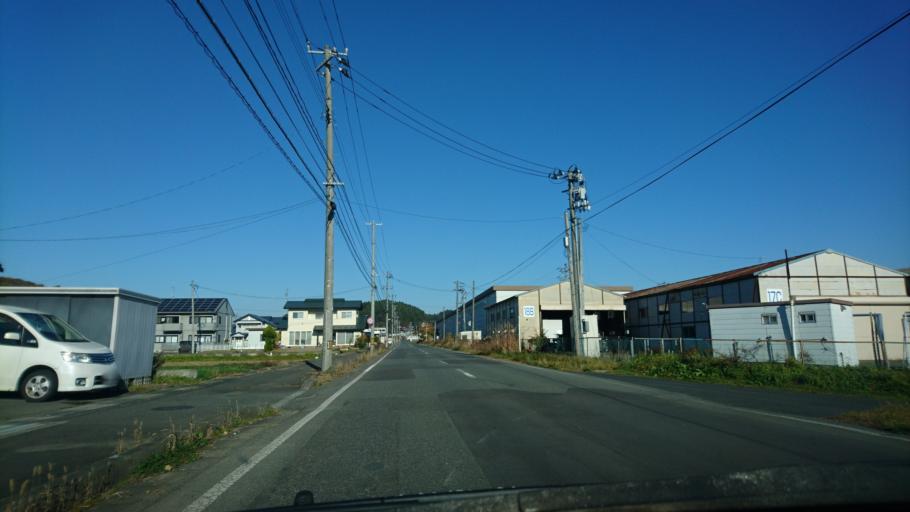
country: JP
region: Iwate
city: Mizusawa
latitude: 39.0364
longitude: 141.1238
